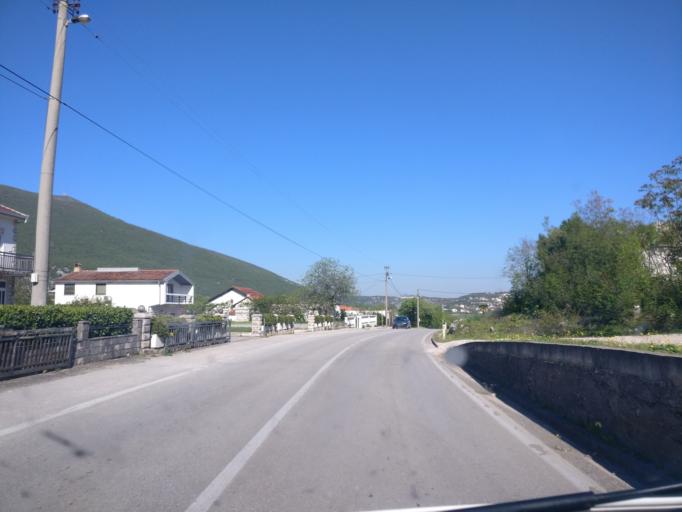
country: BA
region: Federation of Bosnia and Herzegovina
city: Capljina
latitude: 43.1276
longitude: 17.6789
